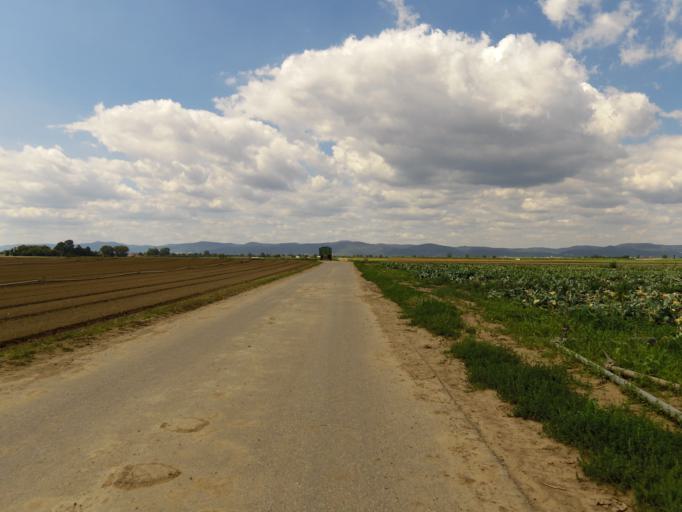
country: DE
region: Rheinland-Pfalz
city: Dannstadt-Schauernheim
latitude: 49.4416
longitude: 8.2930
